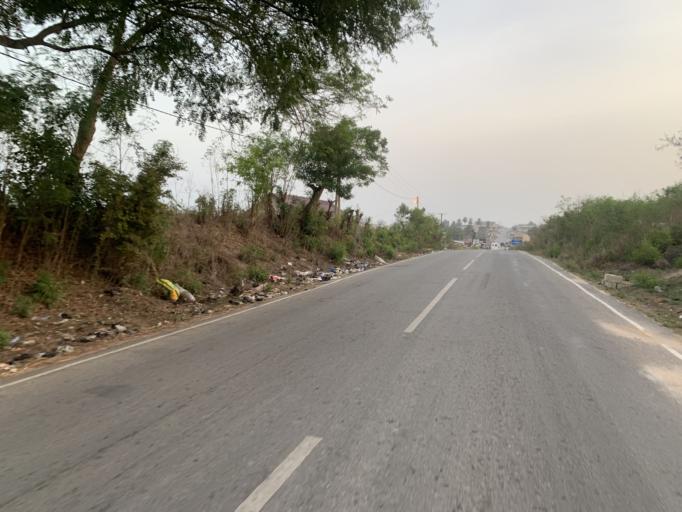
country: GH
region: Central
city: Winneba
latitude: 5.3592
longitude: -0.6099
